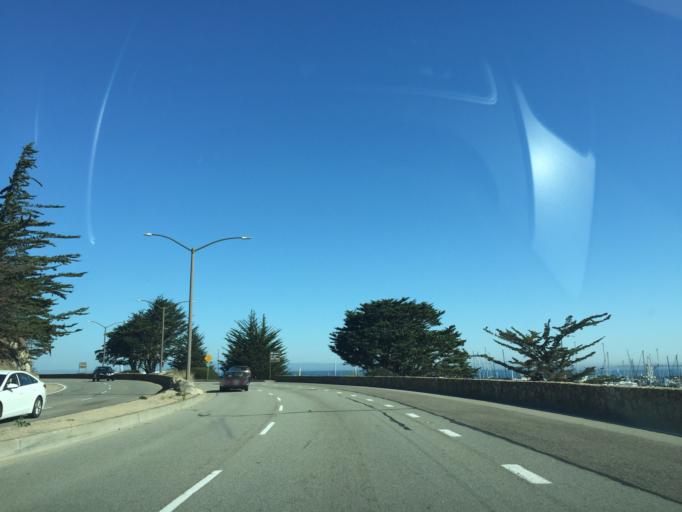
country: US
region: California
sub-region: Monterey County
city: Monterey
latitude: 36.6062
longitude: -121.8945
